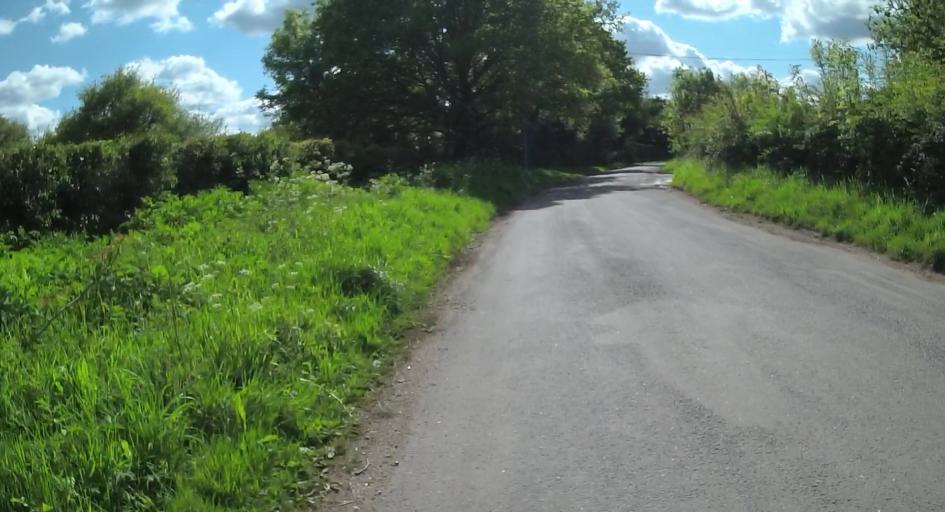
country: GB
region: England
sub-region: Wokingham
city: Swallowfield
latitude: 51.3658
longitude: -0.9516
